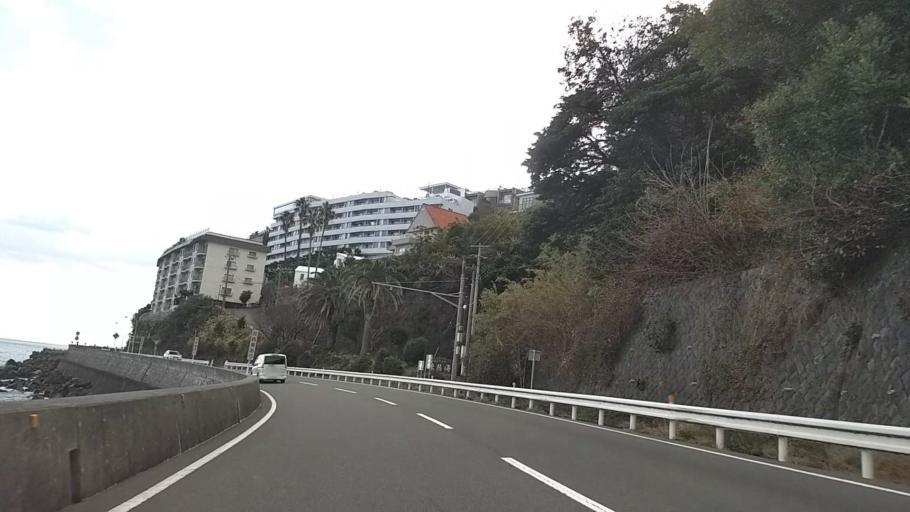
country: JP
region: Kanagawa
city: Yugawara
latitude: 35.1324
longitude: 139.1084
